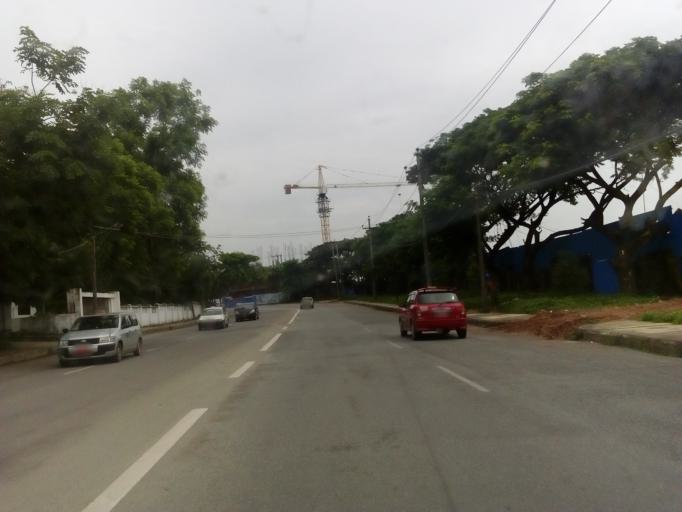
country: MM
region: Yangon
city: Yangon
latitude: 16.8542
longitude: 96.1361
